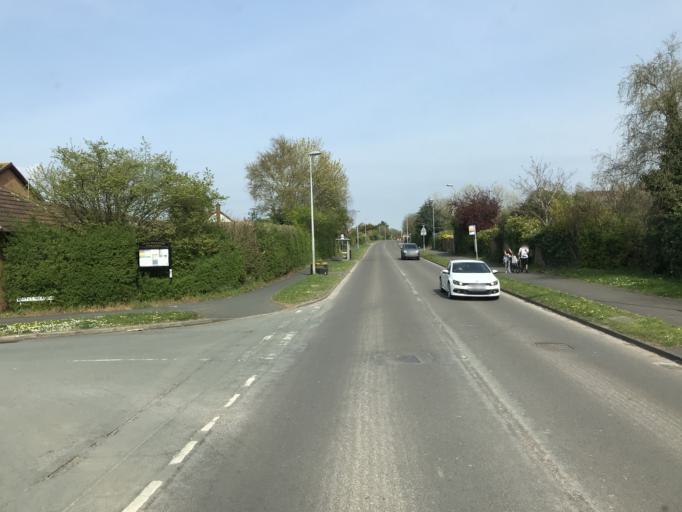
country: GB
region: England
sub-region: Cheshire West and Chester
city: Hoole
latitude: 53.1812
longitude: -2.8595
